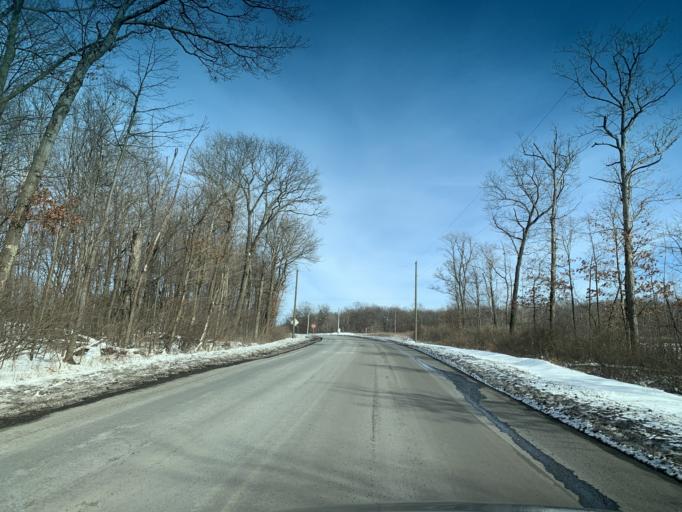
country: US
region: Maryland
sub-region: Allegany County
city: Frostburg
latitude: 39.6196
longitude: -78.9179
